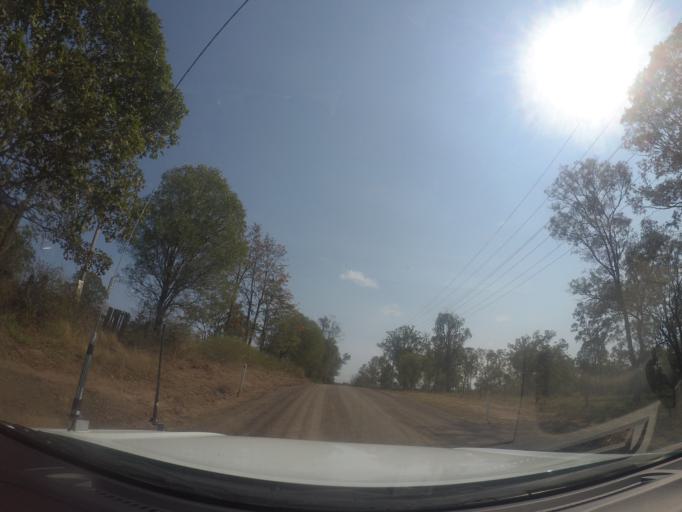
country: AU
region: Queensland
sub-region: Logan
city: Chambers Flat
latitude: -27.7621
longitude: 153.0588
